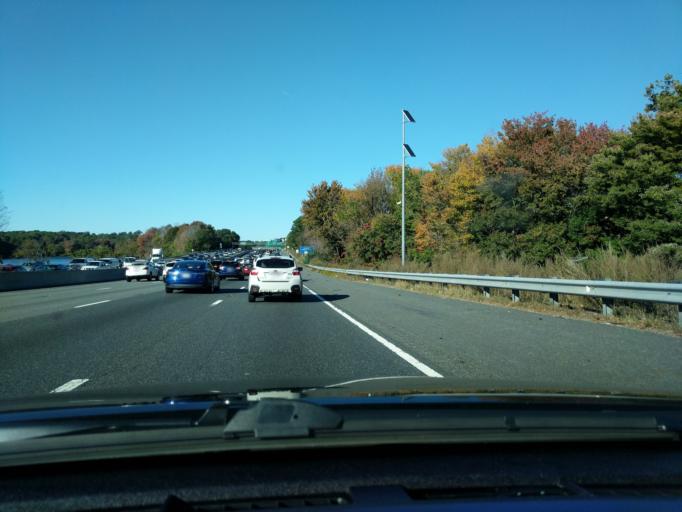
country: US
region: Massachusetts
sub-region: Middlesex County
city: Waltham
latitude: 42.4078
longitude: -71.2585
